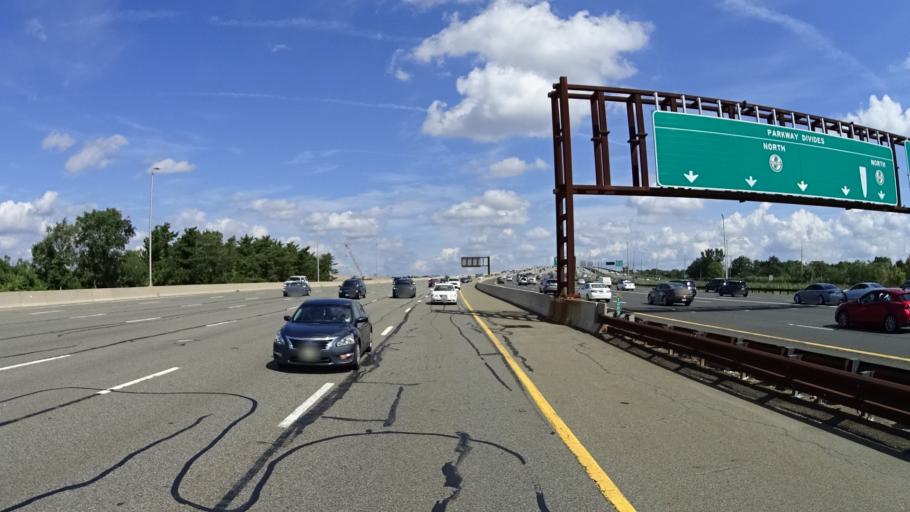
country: US
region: New Jersey
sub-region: Middlesex County
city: South Amboy
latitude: 40.4997
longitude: -74.3012
